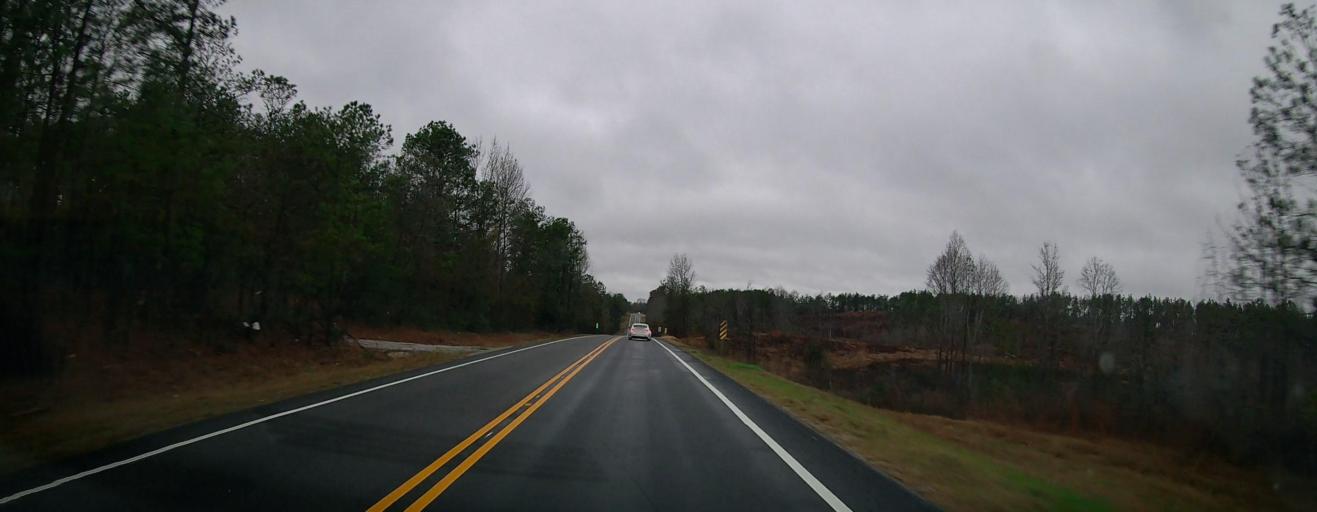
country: US
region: Alabama
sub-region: Chilton County
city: Clanton
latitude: 32.7003
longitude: -86.8054
